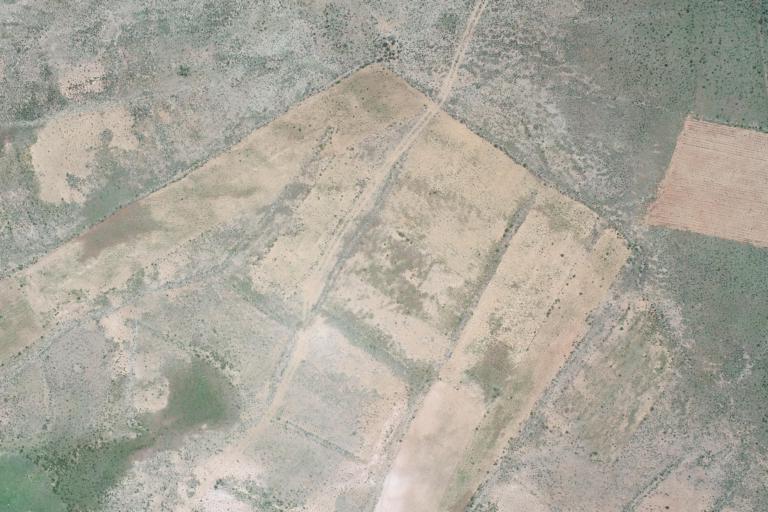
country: BO
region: La Paz
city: Curahuara de Carangas
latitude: -17.3101
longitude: -68.5211
